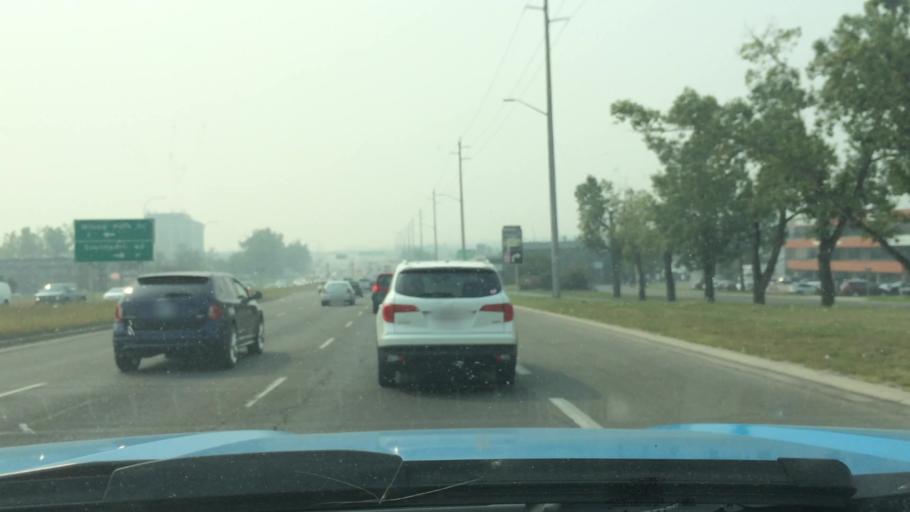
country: CA
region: Alberta
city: Calgary
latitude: 50.9598
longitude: -114.0719
